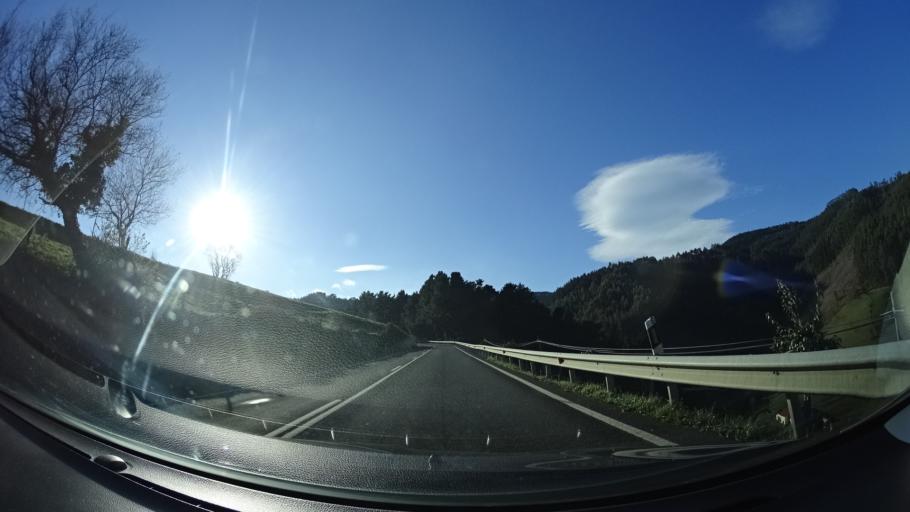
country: ES
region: Basque Country
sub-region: Bizkaia
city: Bermeo
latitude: 43.4160
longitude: -2.7515
